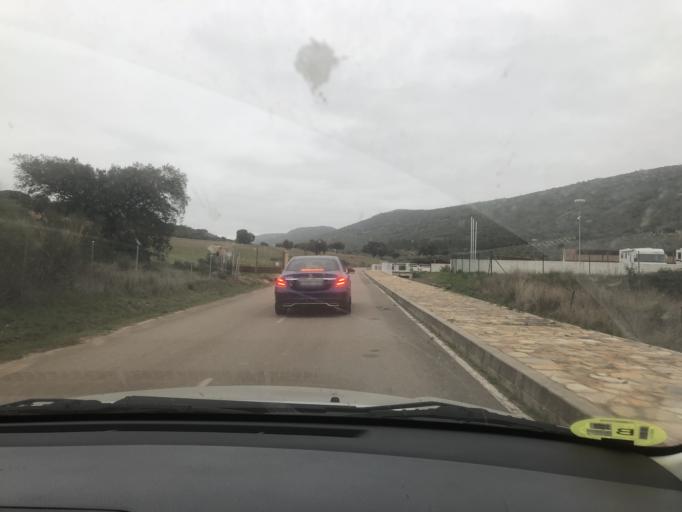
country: ES
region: Castille-La Mancha
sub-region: Provincia de Ciudad Real
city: Navalpino
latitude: 39.3248
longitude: -4.6262
